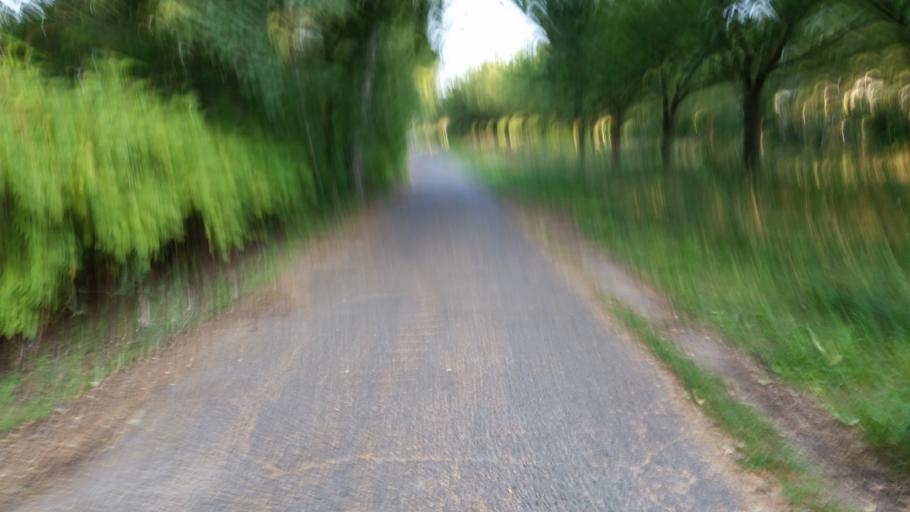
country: DE
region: Berlin
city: Lichterfelde
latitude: 52.4076
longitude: 13.3029
